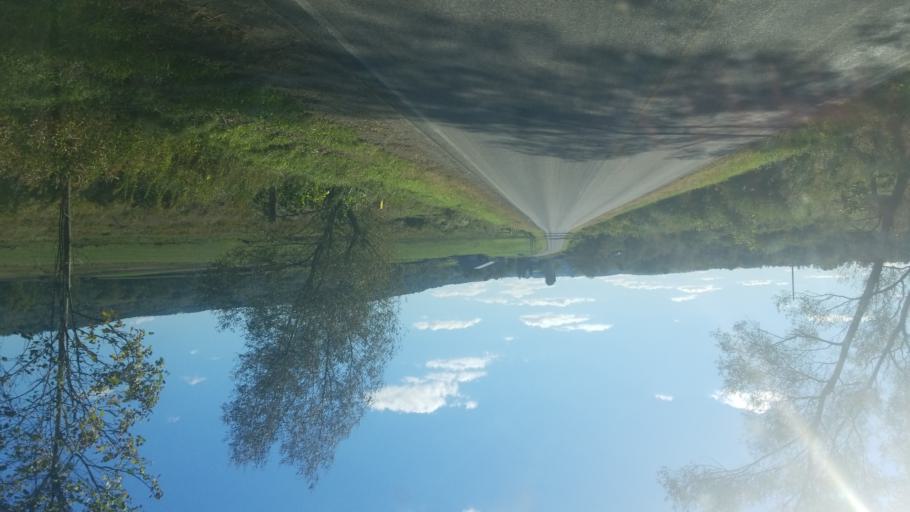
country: US
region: New York
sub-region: Allegany County
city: Cuba
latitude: 42.2745
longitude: -78.2017
